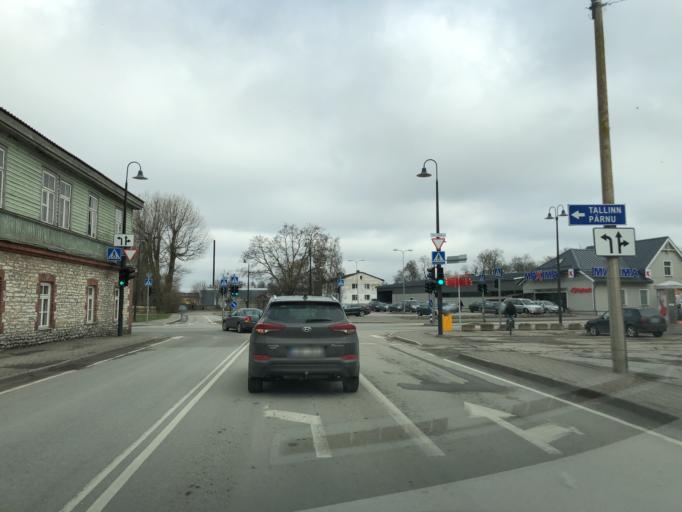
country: EE
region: Laeaene-Virumaa
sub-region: Rakvere linn
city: Rakvere
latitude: 59.3503
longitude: 26.3562
